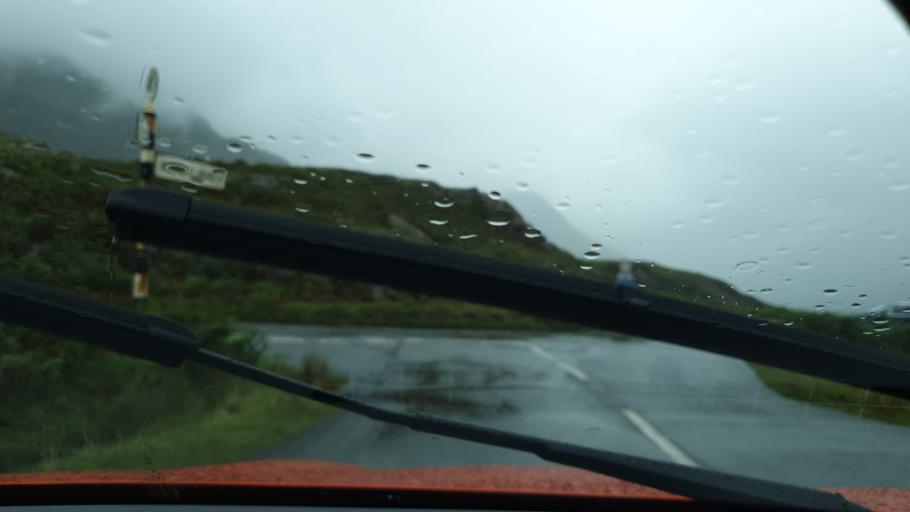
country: GB
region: England
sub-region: Cumbria
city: Seascale
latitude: 54.4368
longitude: -3.3106
